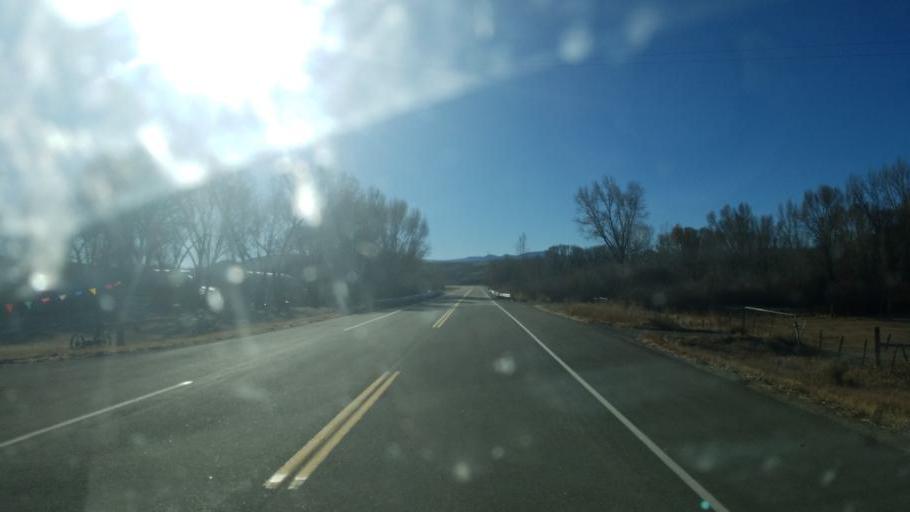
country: US
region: Colorado
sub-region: Gunnison County
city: Gunnison
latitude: 38.5029
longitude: -106.7286
